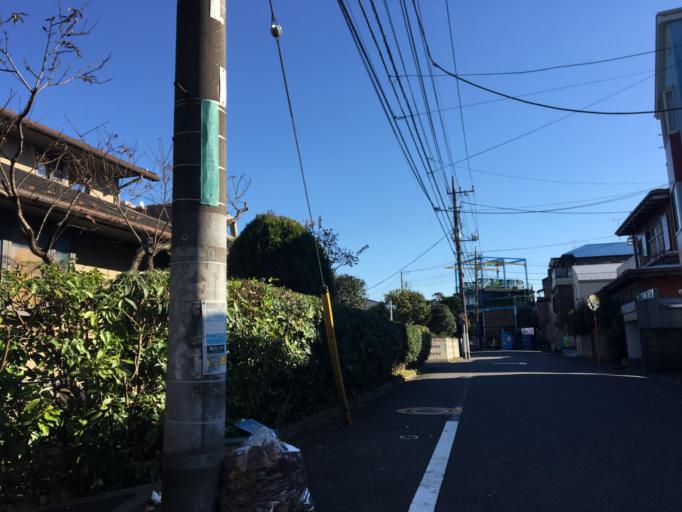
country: JP
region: Tokyo
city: Urayasu
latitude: 35.6950
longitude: 139.9040
